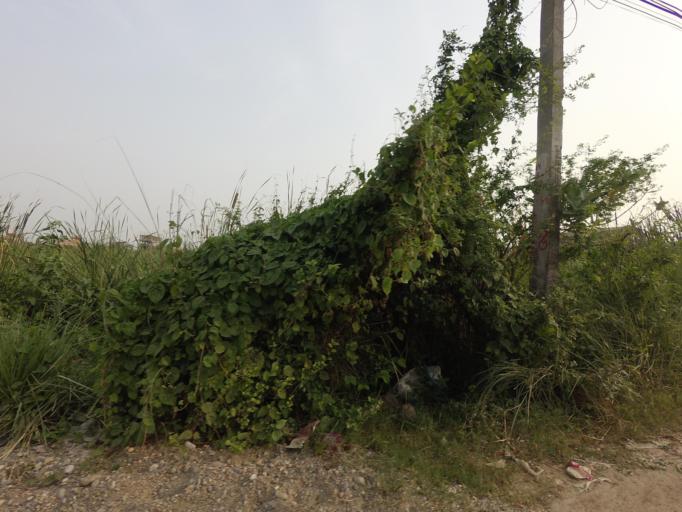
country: NP
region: Western Region
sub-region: Lumbini Zone
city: Bhairahawa
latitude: 27.5081
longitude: 83.4580
